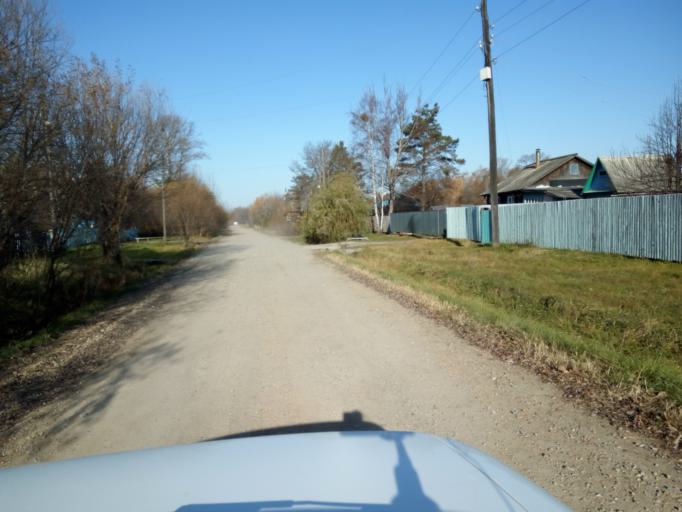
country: RU
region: Primorskiy
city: Lazo
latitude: 45.8775
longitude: 133.6557
